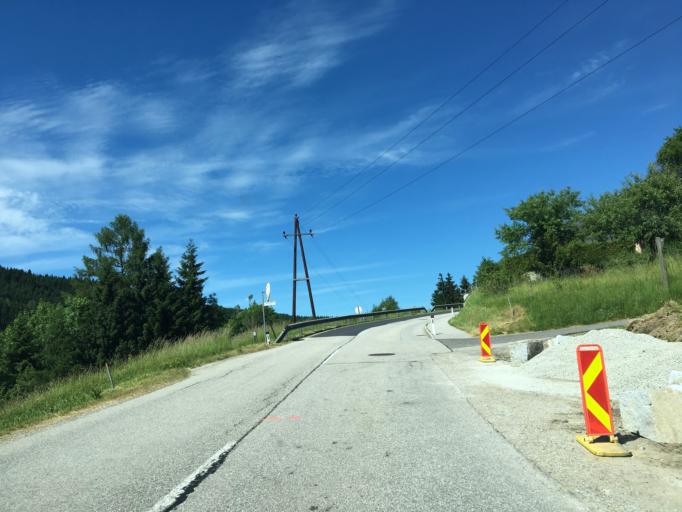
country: AT
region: Upper Austria
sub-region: Politischer Bezirk Urfahr-Umgebung
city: Oberneukirchen
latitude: 48.4304
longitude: 14.2385
